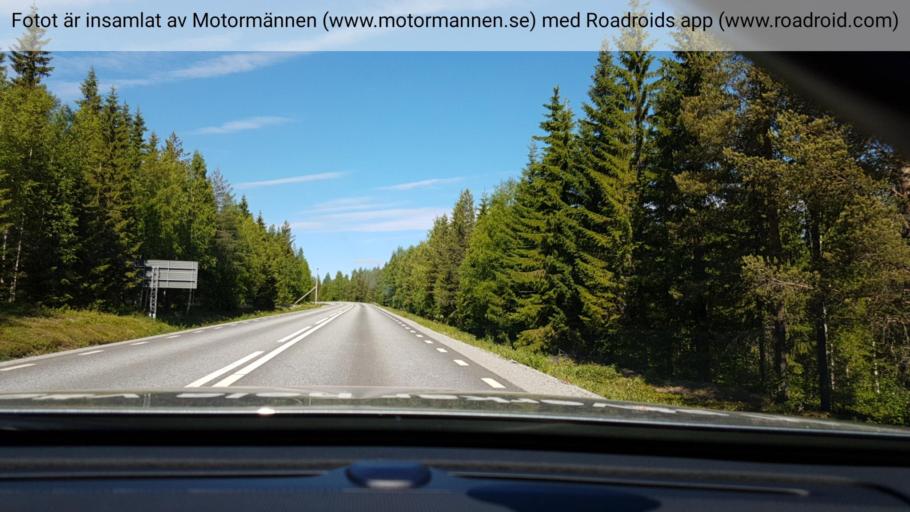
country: SE
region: Vaesterbotten
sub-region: Lycksele Kommun
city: Lycksele
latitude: 64.0704
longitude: 18.3892
